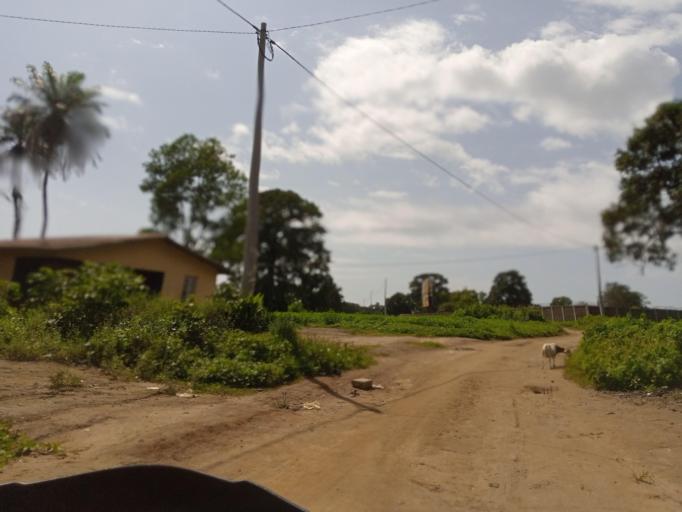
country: SL
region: Northern Province
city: Masoyila
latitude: 8.6090
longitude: -13.2055
